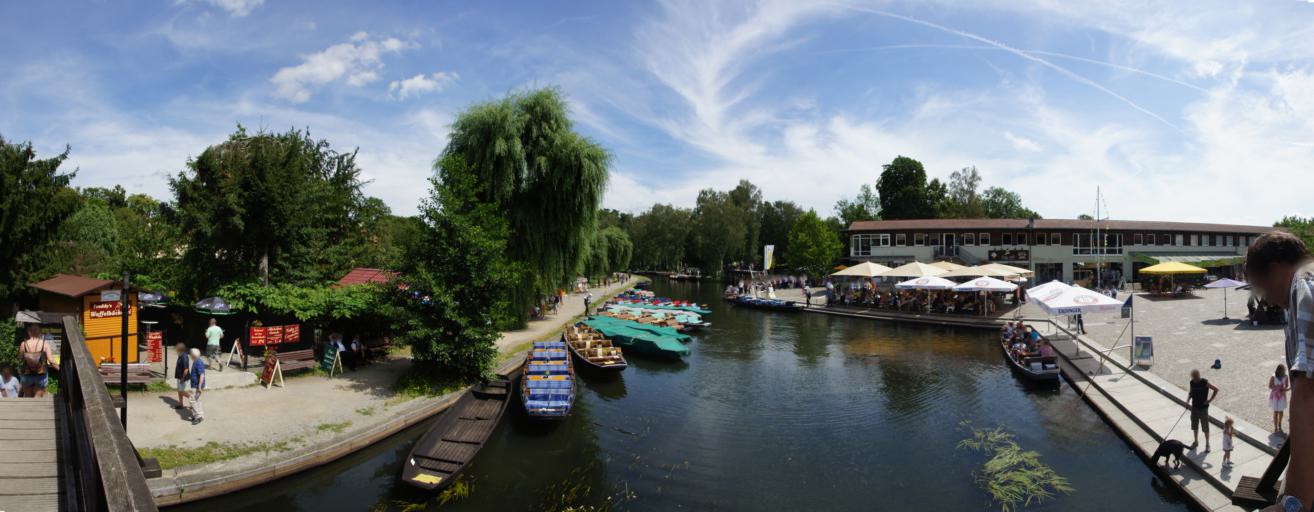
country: DE
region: Brandenburg
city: Lubbenau
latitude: 51.8676
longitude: 13.9731
